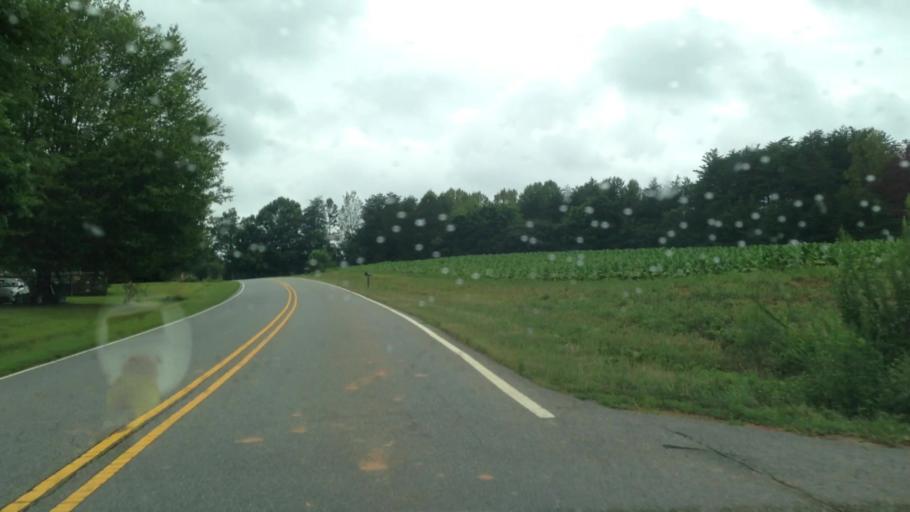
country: US
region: North Carolina
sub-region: Rockingham County
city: Mayodan
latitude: 36.4048
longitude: -80.0432
